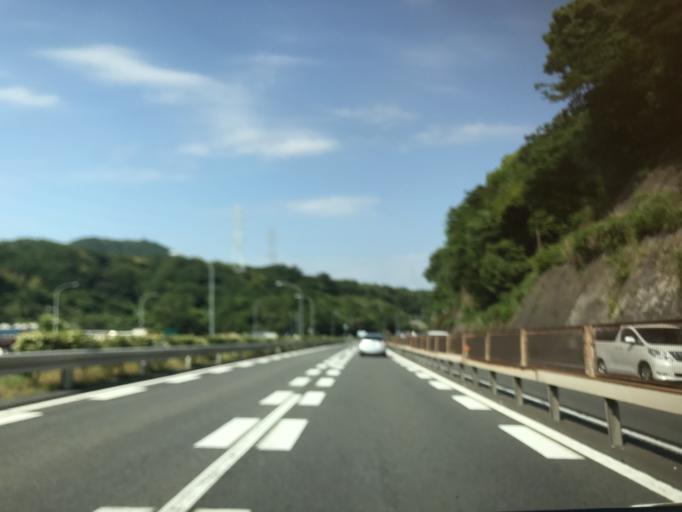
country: JP
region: Kanagawa
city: Ninomiya
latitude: 35.3177
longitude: 139.2690
